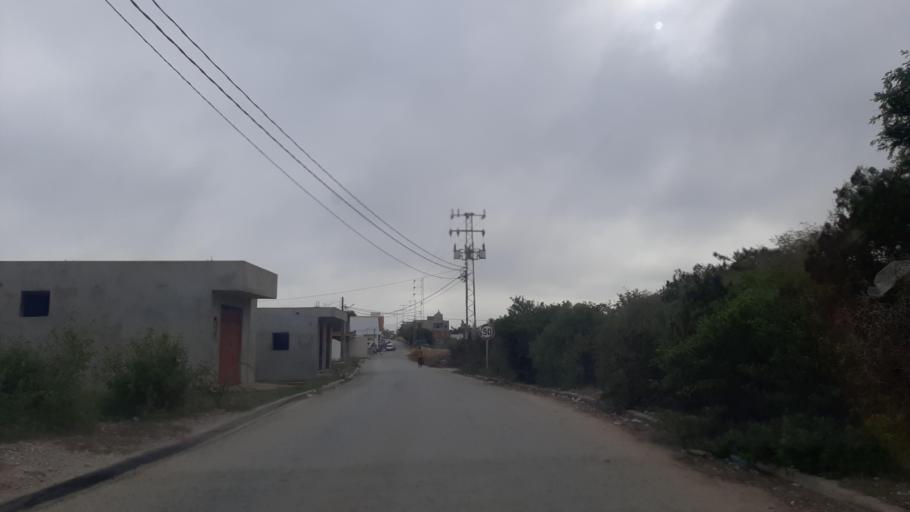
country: TN
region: Nabul
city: Menzel Heurr
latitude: 36.6823
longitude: 10.9268
